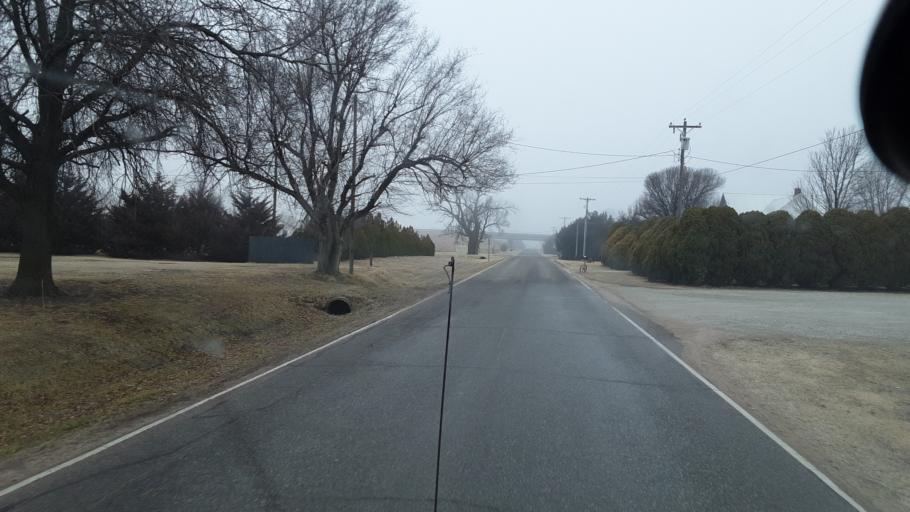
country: US
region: Kansas
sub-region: Reno County
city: Haven
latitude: 37.9410
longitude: -97.8771
